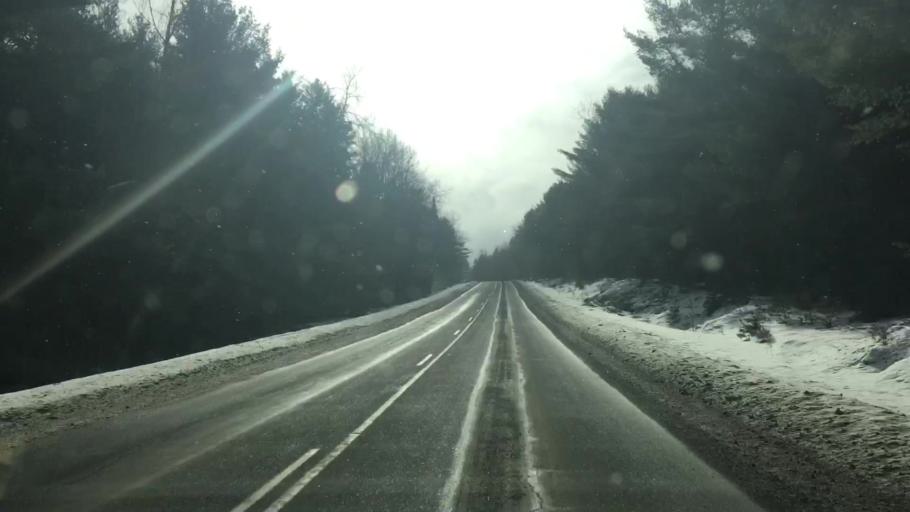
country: US
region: Maine
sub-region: Washington County
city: Calais
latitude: 45.0700
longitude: -67.3313
